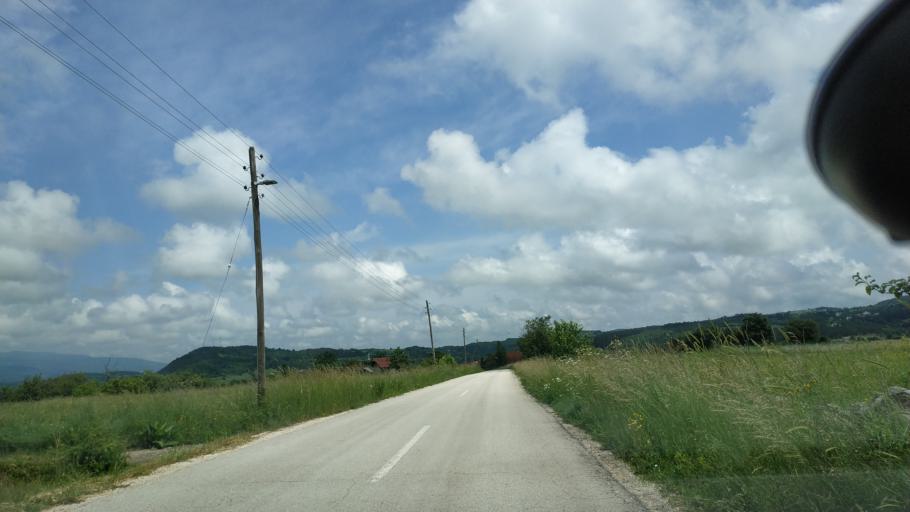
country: RS
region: Central Serbia
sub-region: Zajecarski Okrug
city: Boljevac
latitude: 43.8231
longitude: 21.9556
